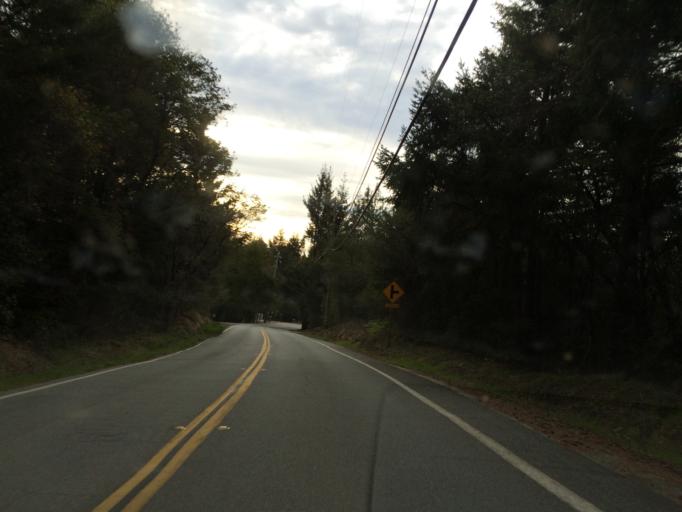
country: US
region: California
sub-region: Santa Cruz County
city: Felton
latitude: 37.0462
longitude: -122.1114
